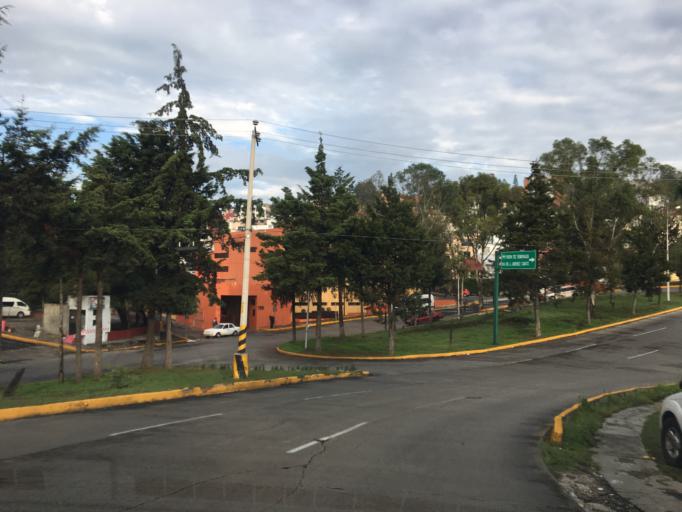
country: MX
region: Mexico
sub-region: Naucalpan de Juarez
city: Rincon Verde
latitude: 19.5173
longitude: -99.2709
